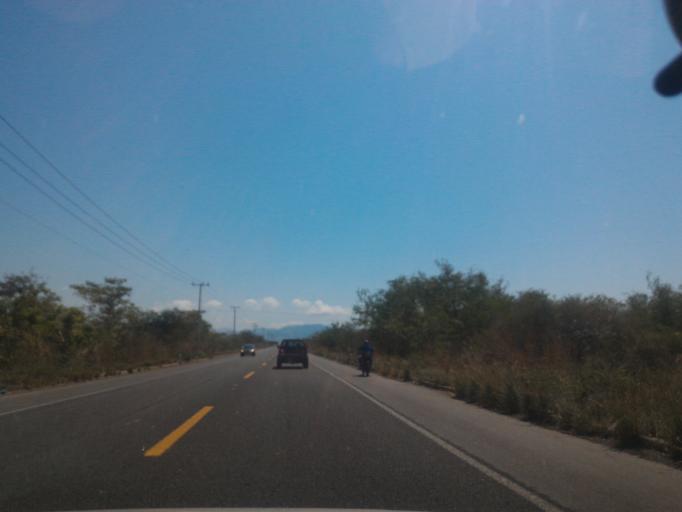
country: MX
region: Michoacan
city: Coahuayana Viejo
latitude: 18.7667
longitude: -103.7355
